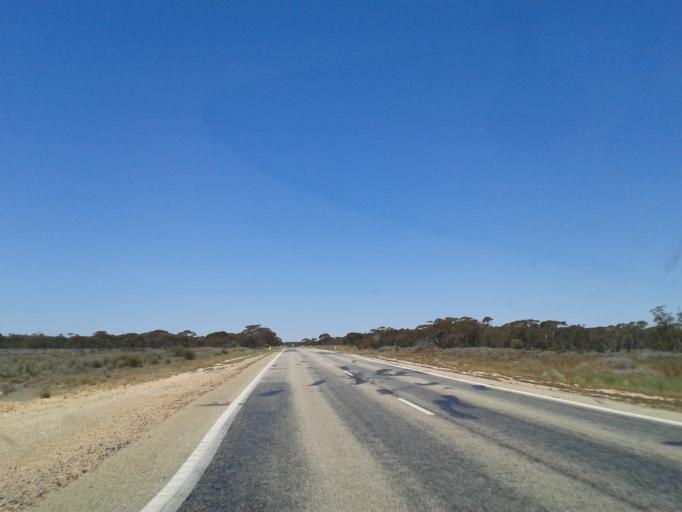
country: AU
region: New South Wales
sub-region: Wentworth
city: Gol Gol
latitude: -34.4215
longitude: 142.4496
